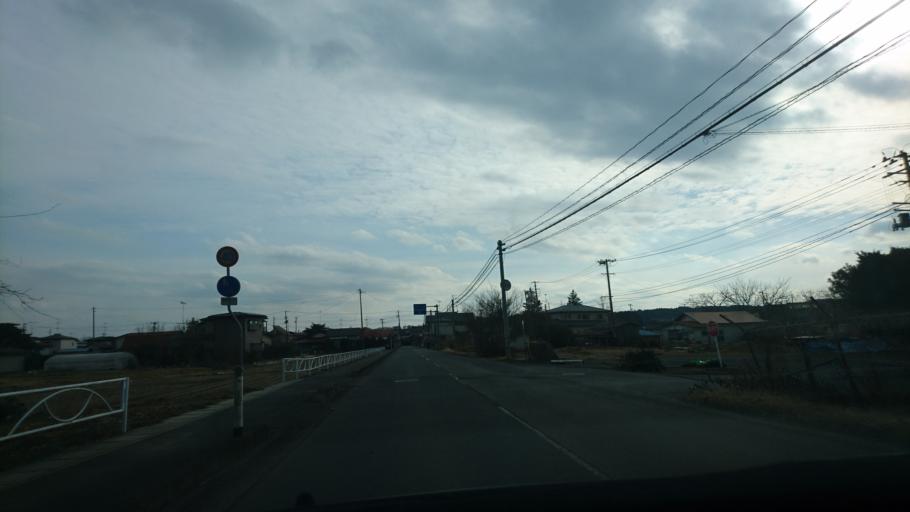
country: JP
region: Iwate
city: Ichinoseki
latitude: 38.8499
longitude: 141.1721
